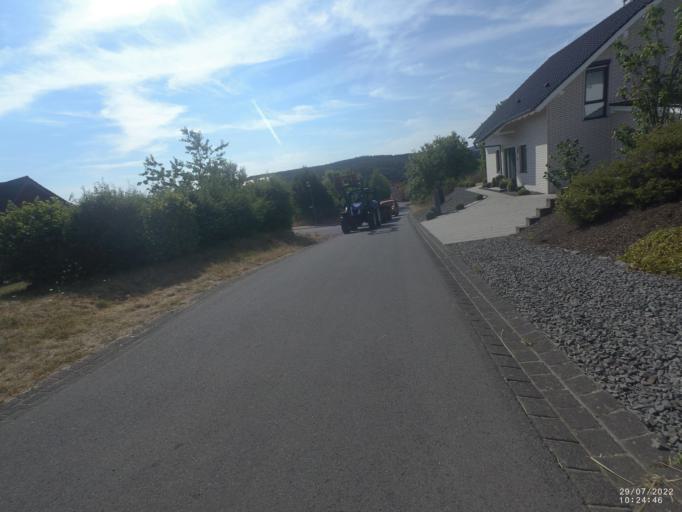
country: DE
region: Rheinland-Pfalz
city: Gerolstein
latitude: 50.2175
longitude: 6.6304
